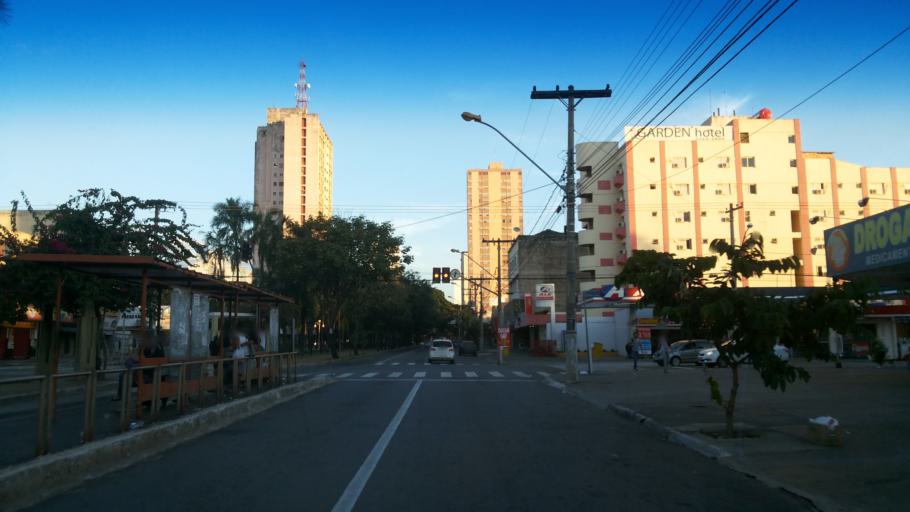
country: BR
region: Goias
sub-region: Goiania
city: Goiania
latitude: -16.6683
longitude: -49.2604
